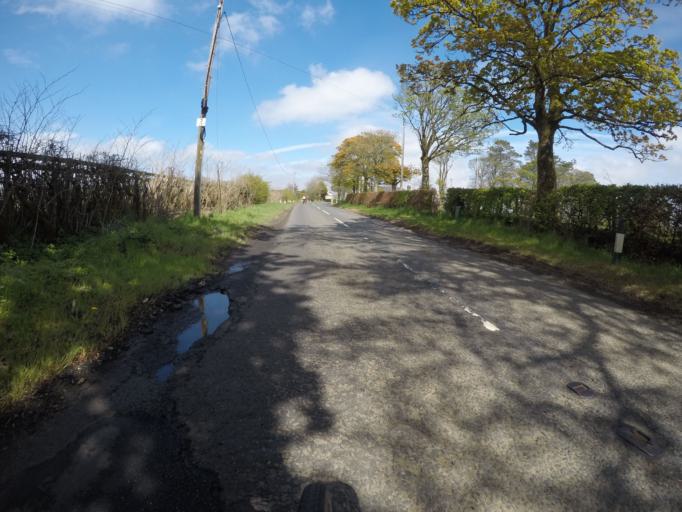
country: GB
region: Scotland
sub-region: East Ayrshire
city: Stewarton
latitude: 55.6936
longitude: -4.4916
